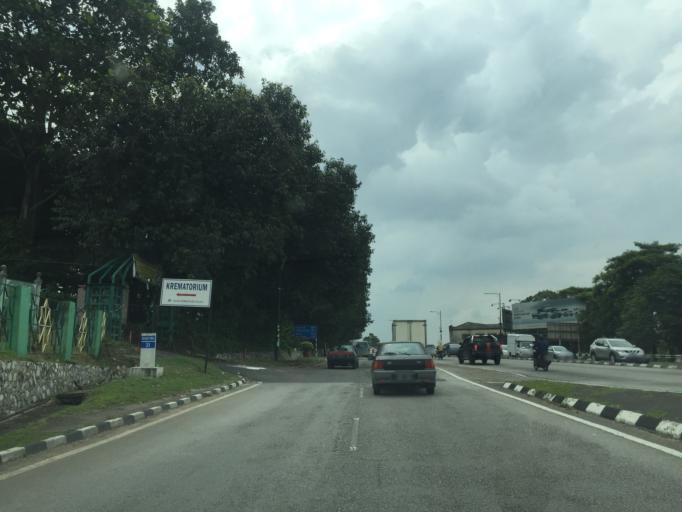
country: MY
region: Selangor
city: Klang
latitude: 3.0350
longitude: 101.4424
